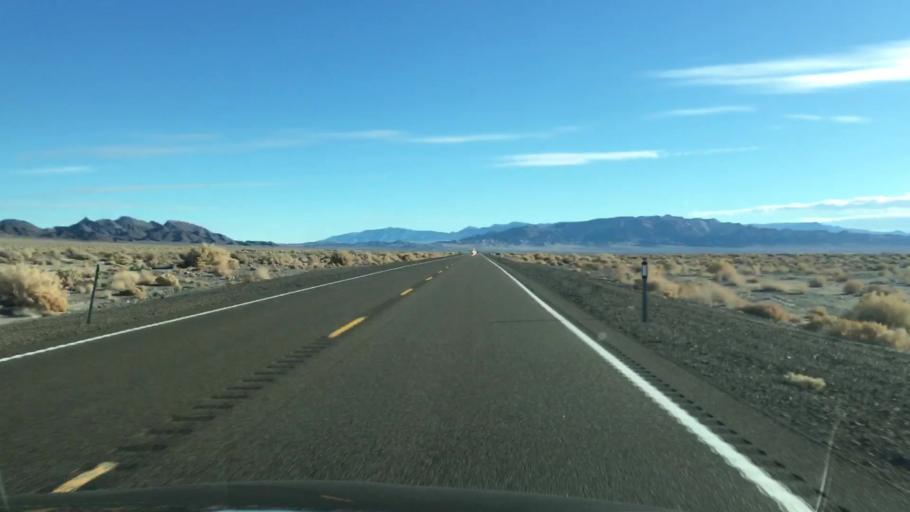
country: US
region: Nevada
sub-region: Nye County
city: Tonopah
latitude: 38.1091
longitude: -117.9278
